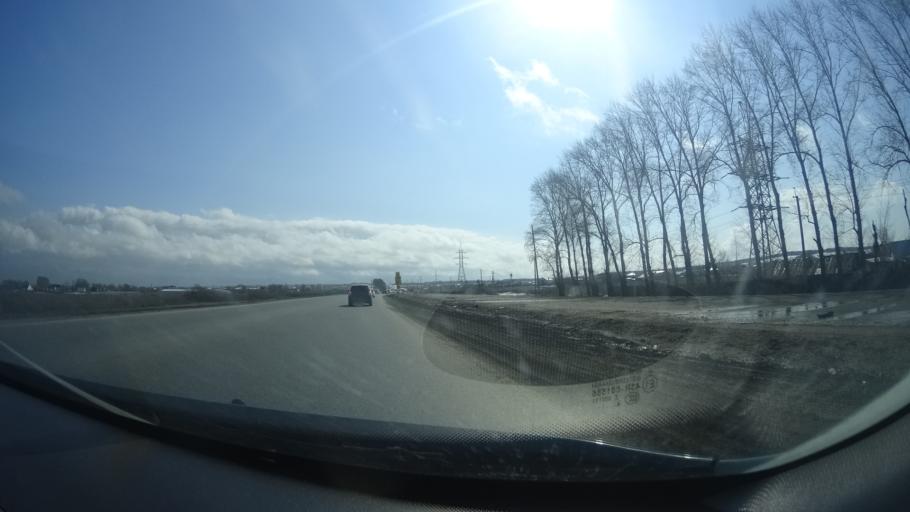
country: RU
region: Bashkortostan
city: Mikhaylovka
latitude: 54.8719
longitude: 55.7366
